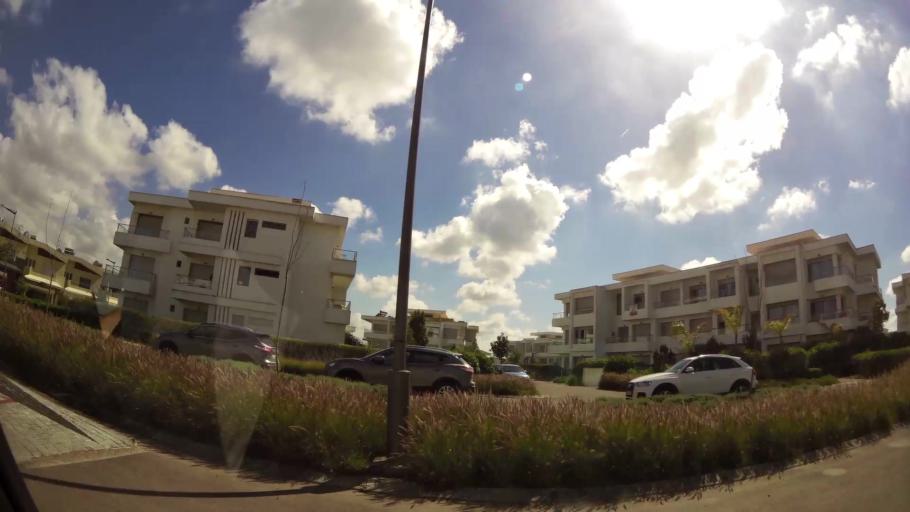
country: MA
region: Grand Casablanca
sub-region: Nouaceur
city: Bouskoura
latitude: 33.4689
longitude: -7.6054
